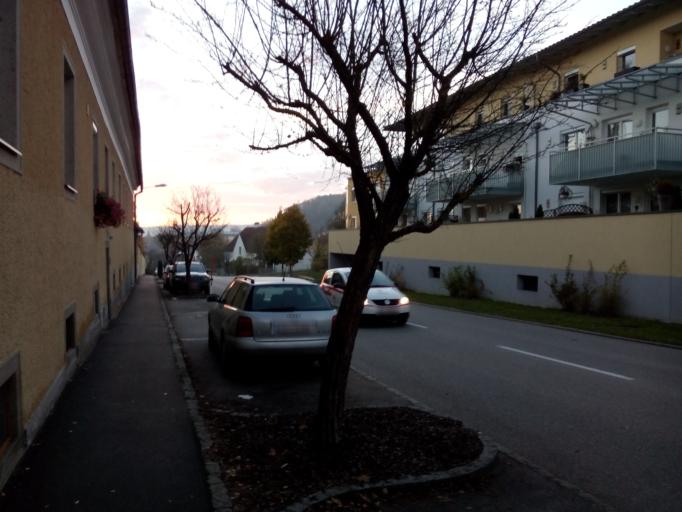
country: AT
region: Upper Austria
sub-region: Politischer Bezirk Linz-Land
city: Sankt Florian
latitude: 48.2059
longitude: 14.3759
